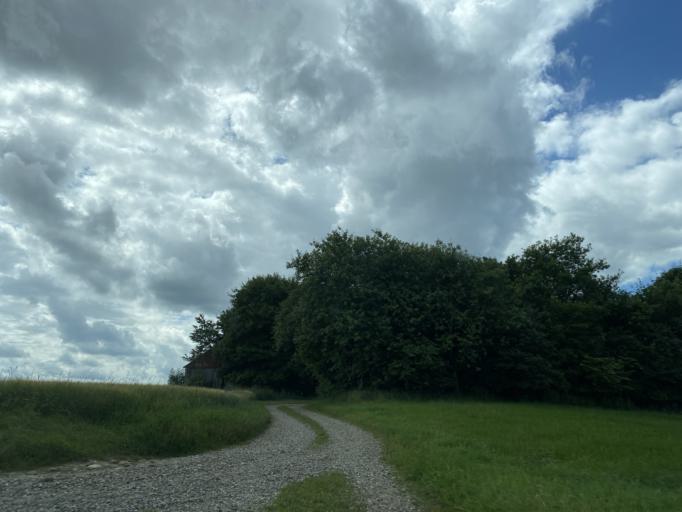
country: DK
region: Central Jutland
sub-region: Silkeborg Kommune
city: Silkeborg
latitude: 56.2114
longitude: 9.5749
